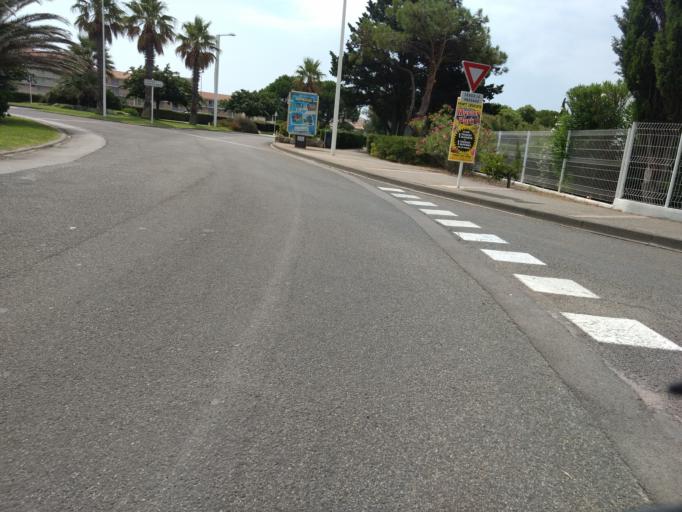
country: FR
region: Languedoc-Roussillon
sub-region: Departement de l'Aude
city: Leucate
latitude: 42.8632
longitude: 3.0427
